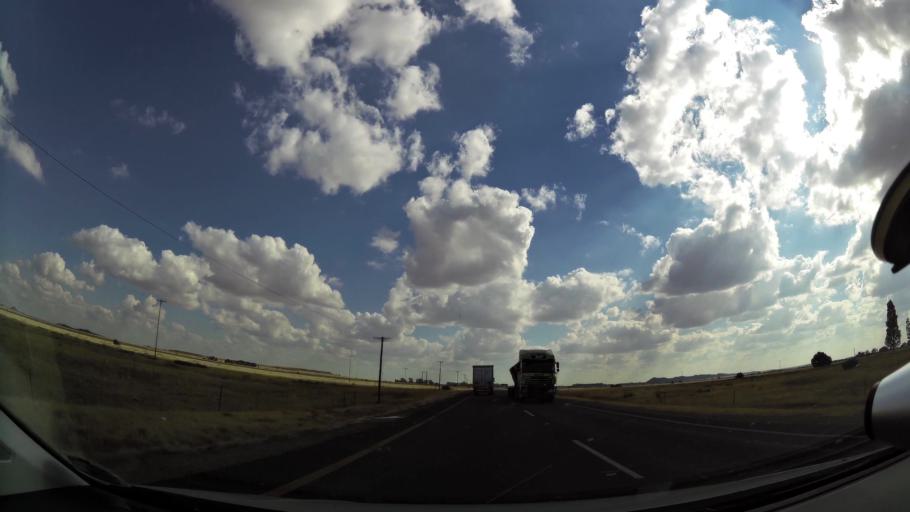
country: ZA
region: Orange Free State
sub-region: Xhariep District Municipality
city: Koffiefontein
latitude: -29.1265
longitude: 25.4725
